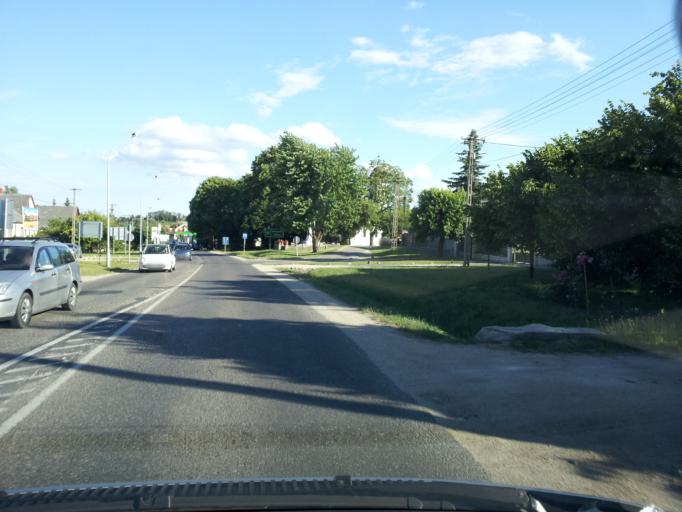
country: HU
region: Veszprem
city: Zirc
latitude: 47.2570
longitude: 17.8758
